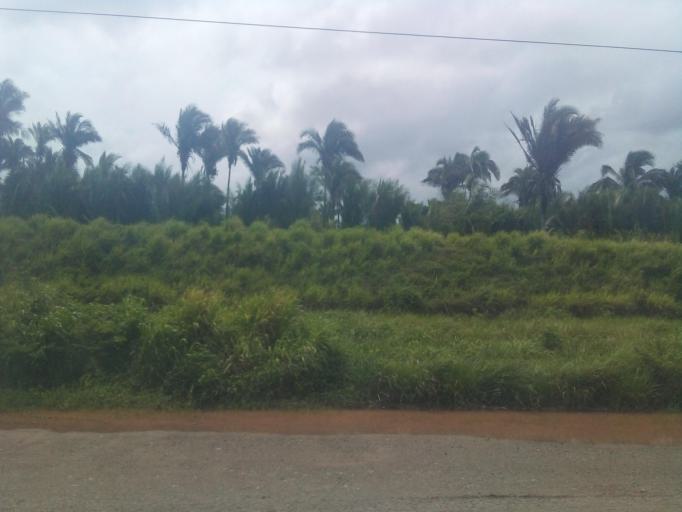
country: BR
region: Maranhao
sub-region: Arari
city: Arari
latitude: -3.5548
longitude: -44.6664
